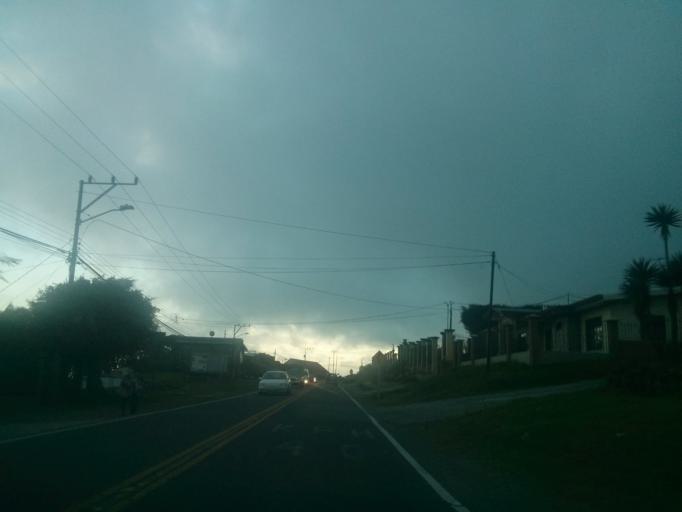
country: CR
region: Cartago
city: Cot
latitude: 9.8871
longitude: -83.8647
